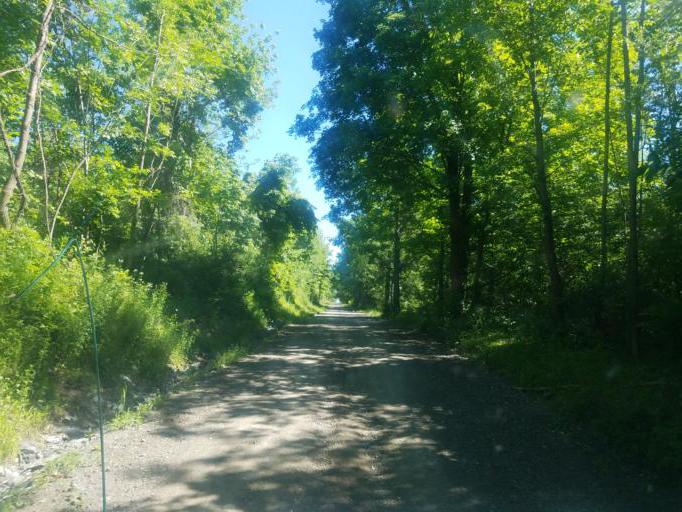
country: US
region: New York
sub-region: Ontario County
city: Naples
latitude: 42.6700
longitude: -77.3395
